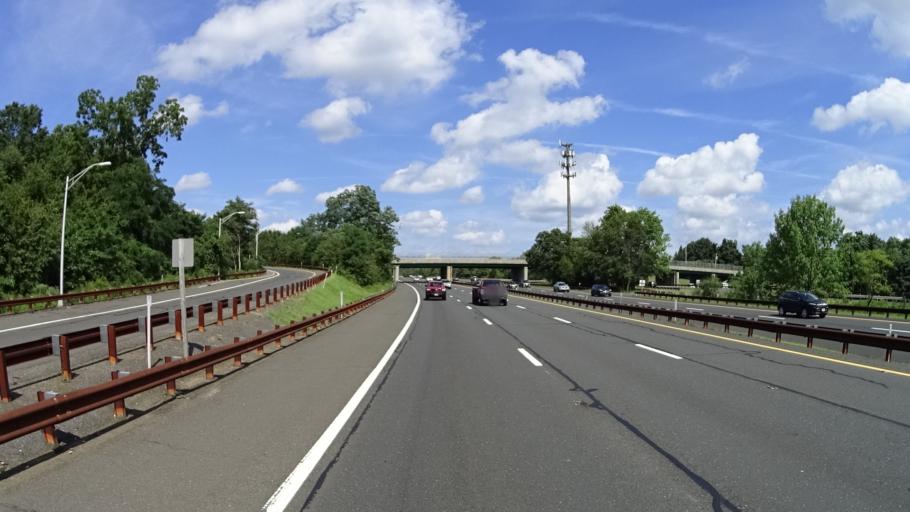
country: US
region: New Jersey
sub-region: Monmouth County
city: Lincroft
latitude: 40.3734
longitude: -74.1465
